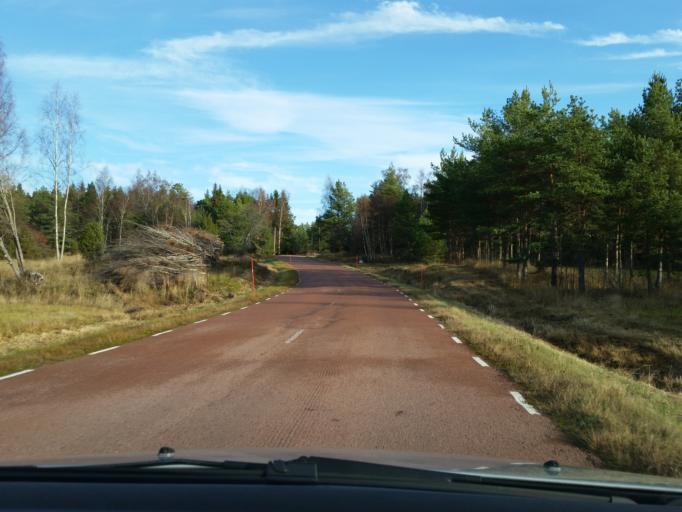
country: AX
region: Alands landsbygd
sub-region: Saltvik
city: Saltvik
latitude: 60.3221
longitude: 20.0778
